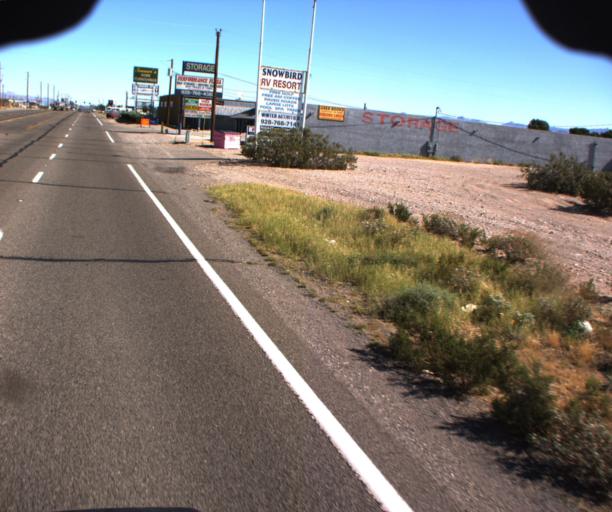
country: US
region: Arizona
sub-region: Mohave County
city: Mohave Valley
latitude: 34.9929
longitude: -114.5979
